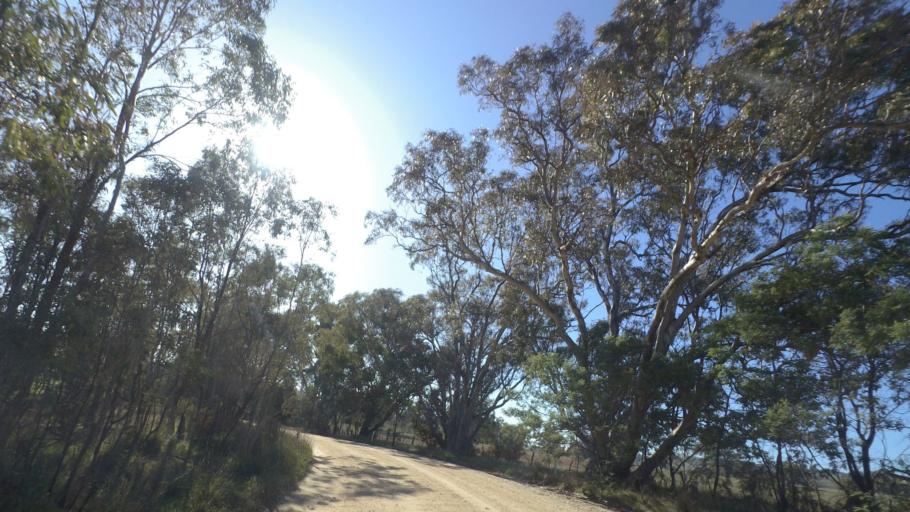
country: AU
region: Victoria
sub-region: Mount Alexander
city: Castlemaine
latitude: -37.1092
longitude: 144.4193
